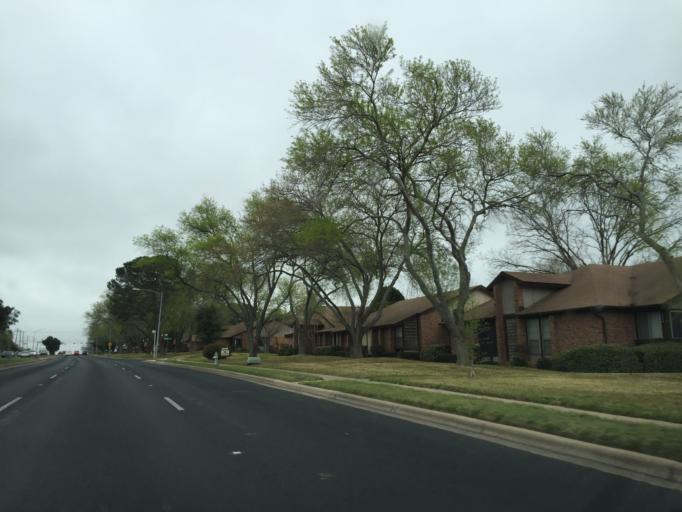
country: US
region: Texas
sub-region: Travis County
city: Wells Branch
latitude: 30.3876
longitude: -97.6986
